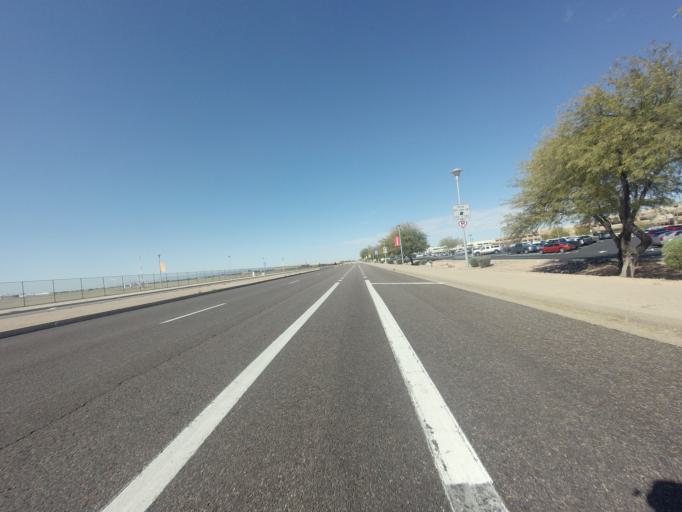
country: US
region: Arizona
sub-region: Maricopa County
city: Mesa
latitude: 33.4665
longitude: -111.7204
